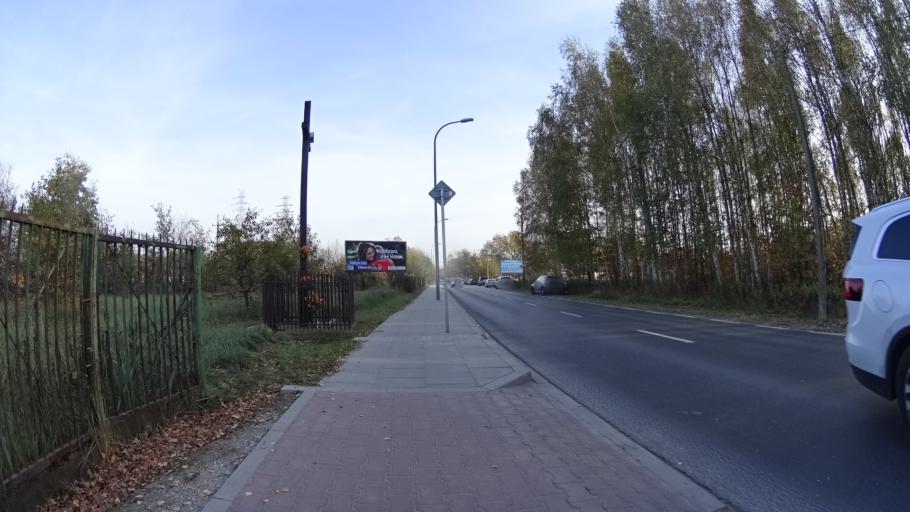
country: PL
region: Masovian Voivodeship
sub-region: Powiat warszawski zachodni
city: Lomianki
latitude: 52.2970
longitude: 20.8898
